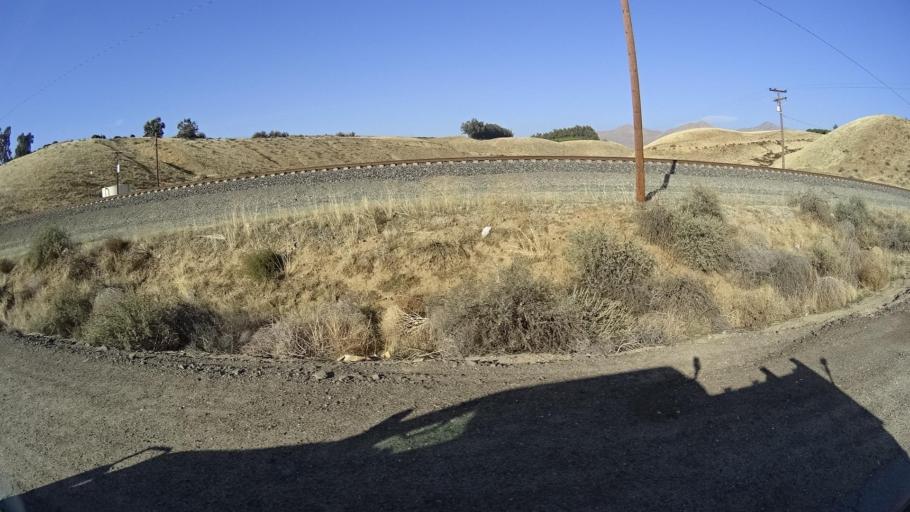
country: US
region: California
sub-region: Kern County
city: Arvin
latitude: 35.3293
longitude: -118.7594
